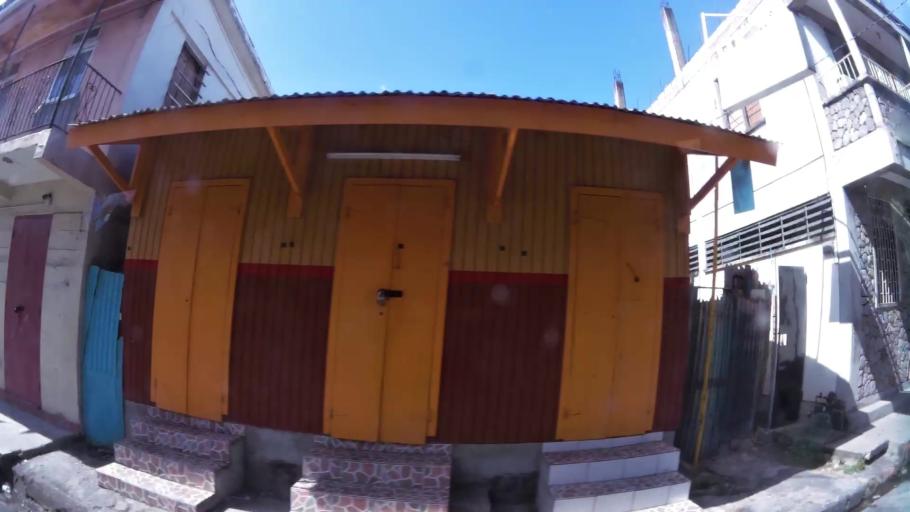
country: DM
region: Saint George
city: Roseau
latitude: 15.2998
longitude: -61.3871
